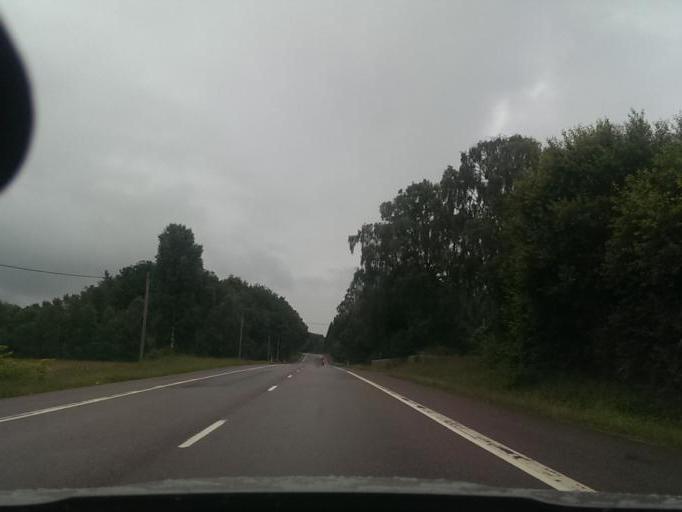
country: SE
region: Skane
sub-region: Orkelljunga Kommun
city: OErkelljunga
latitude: 56.2987
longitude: 13.3384
